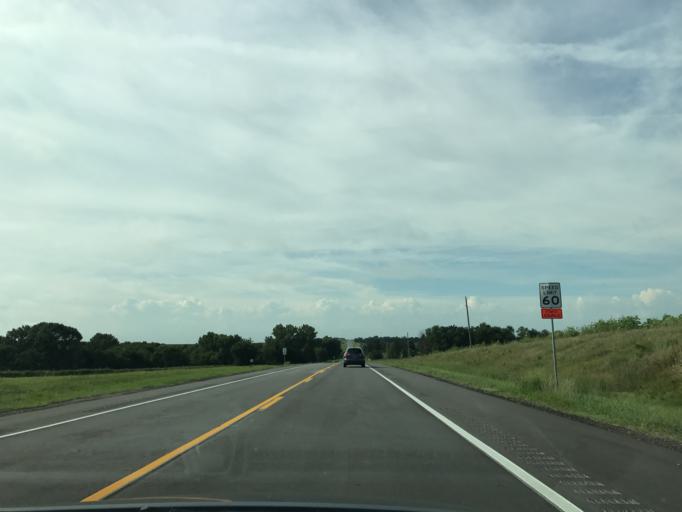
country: US
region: Nebraska
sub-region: Seward County
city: Seward
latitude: 40.8427
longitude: -97.1018
